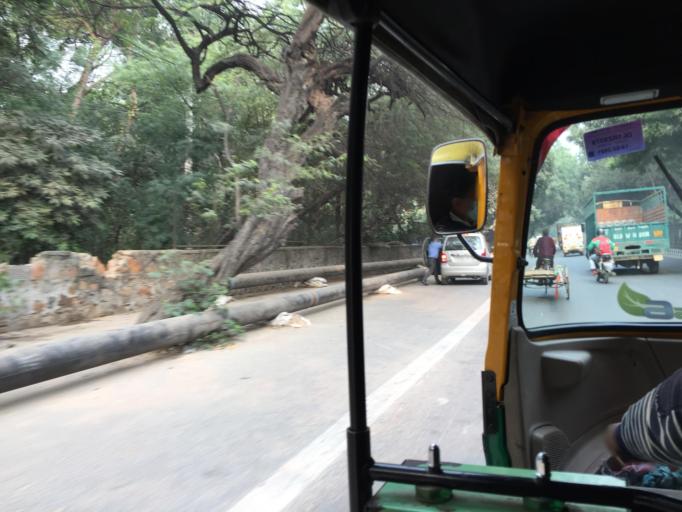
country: IN
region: NCT
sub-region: New Delhi
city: New Delhi
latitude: 28.5152
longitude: 77.1870
